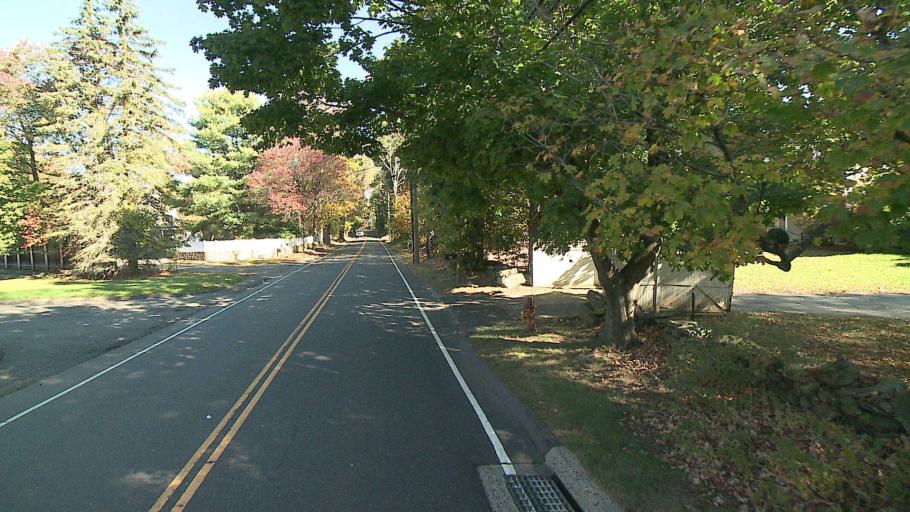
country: US
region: Connecticut
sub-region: Fairfield County
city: Westport
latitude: 41.1708
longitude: -73.3511
